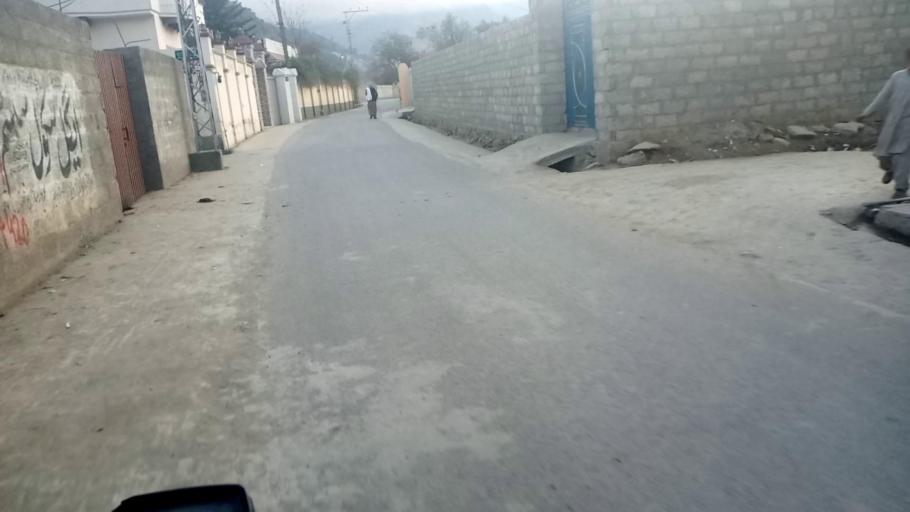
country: PK
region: Khyber Pakhtunkhwa
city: Saidu Sharif
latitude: 34.7398
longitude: 72.3372
